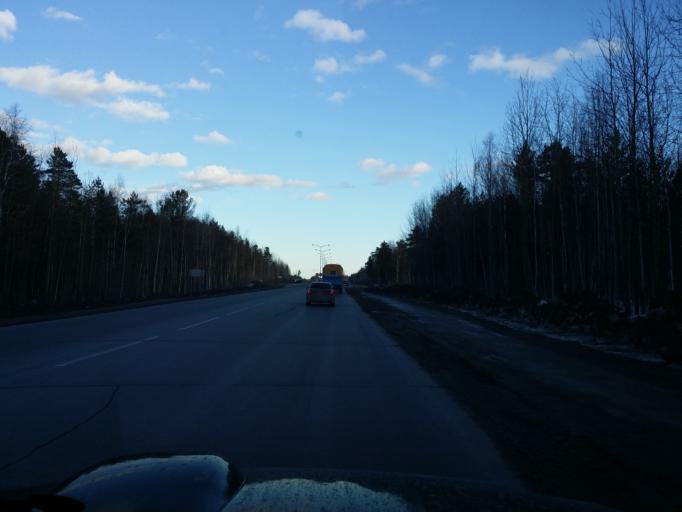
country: RU
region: Khanty-Mansiyskiy Avtonomnyy Okrug
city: Nizhnevartovsk
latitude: 61.0122
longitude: 76.3988
